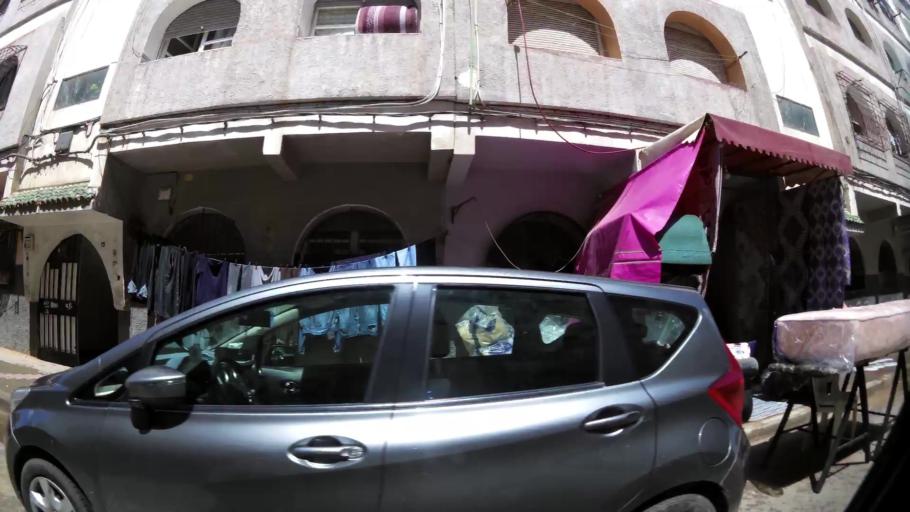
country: MA
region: Grand Casablanca
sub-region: Mediouna
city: Tit Mellil
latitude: 33.5384
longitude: -7.5504
